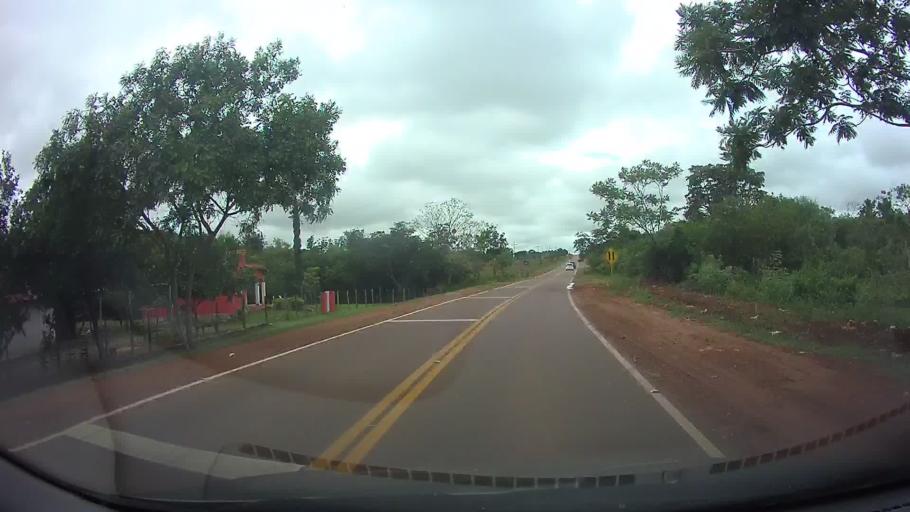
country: PY
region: Paraguari
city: Carapegua
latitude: -25.7992
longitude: -57.1932
